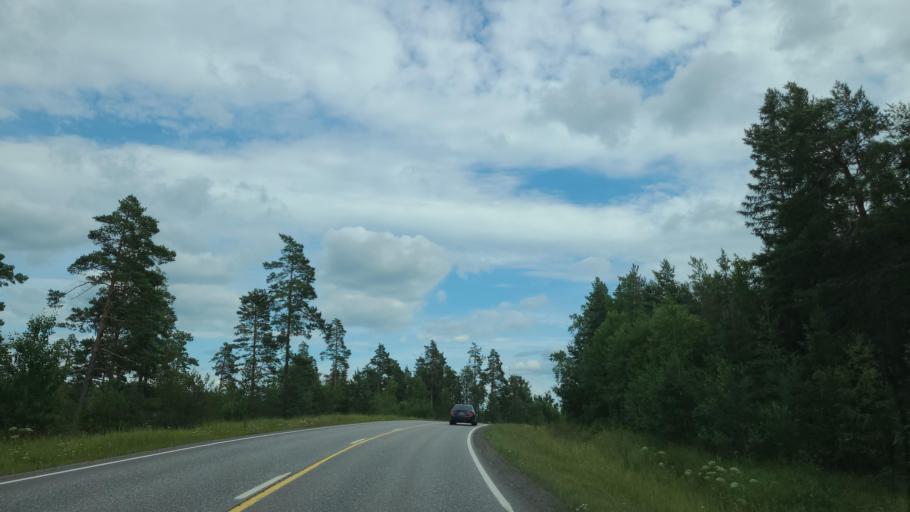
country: FI
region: Varsinais-Suomi
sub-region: Turku
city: Rymaettylae
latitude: 60.3901
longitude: 21.9121
